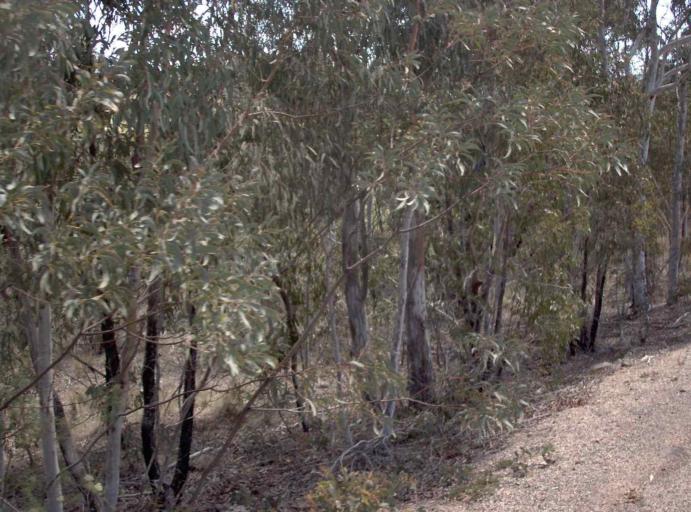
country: AU
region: New South Wales
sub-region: Snowy River
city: Jindabyne
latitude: -37.0736
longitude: 148.2817
